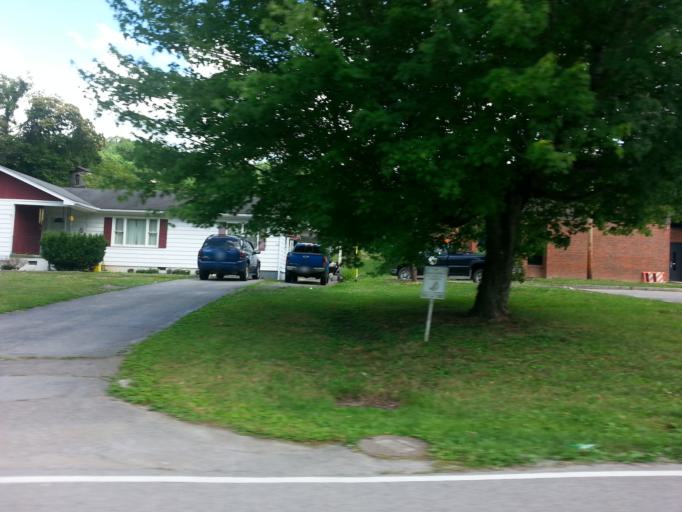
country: US
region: Kentucky
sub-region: Harlan County
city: Harlan
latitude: 36.8838
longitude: -83.2899
